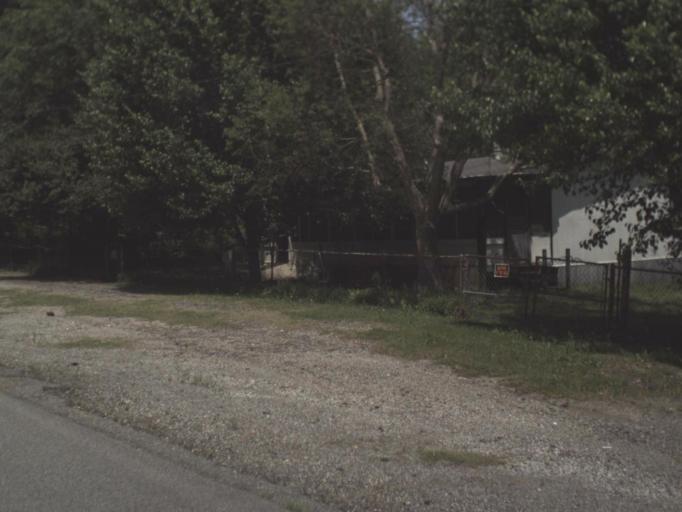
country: US
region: Florida
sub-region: Escambia County
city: Molino
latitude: 30.7535
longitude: -87.3770
